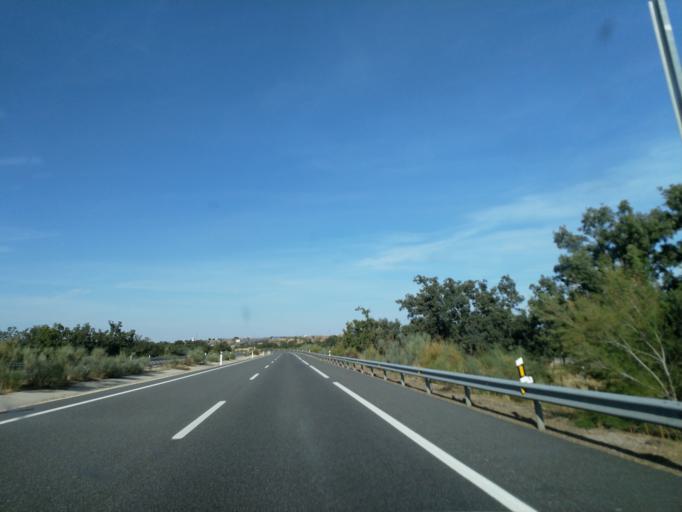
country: ES
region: Castille and Leon
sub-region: Provincia de Segovia
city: Villacastin
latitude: 40.7567
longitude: -4.4477
